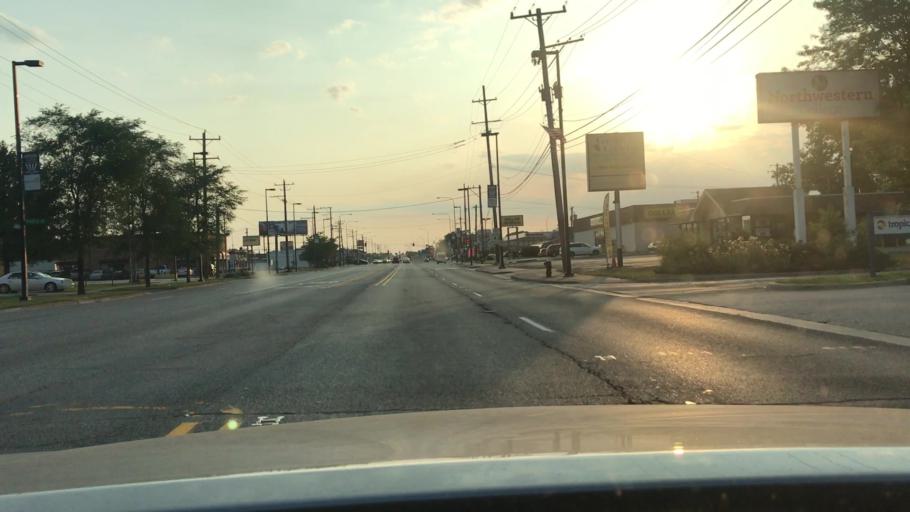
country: US
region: Illinois
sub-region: Cook County
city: Bridgeview
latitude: 41.7483
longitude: -87.7959
